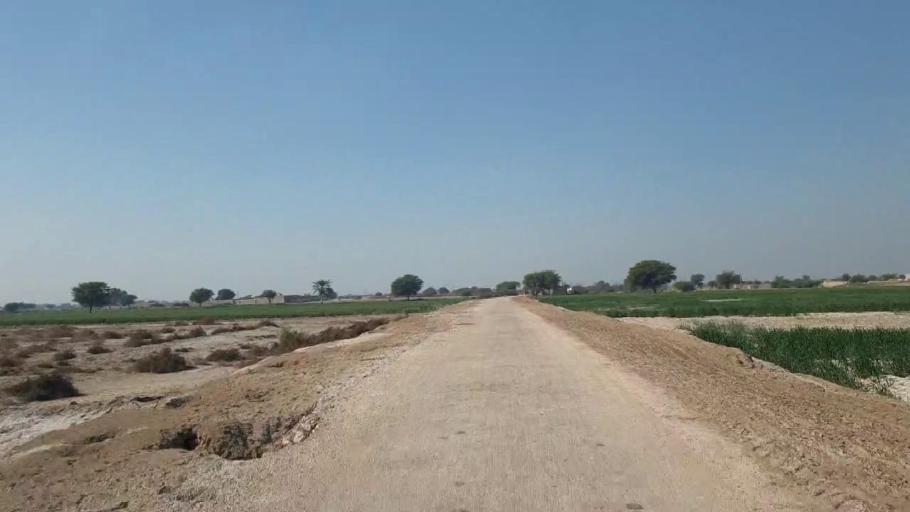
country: PK
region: Sindh
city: Shahpur Chakar
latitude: 26.1182
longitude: 68.6089
